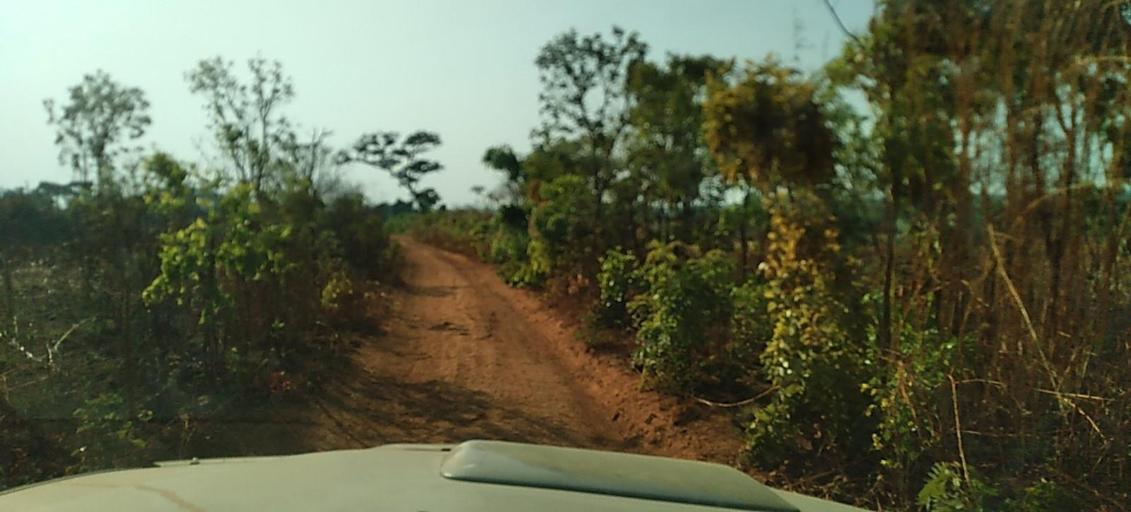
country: ZM
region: North-Western
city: Kasempa
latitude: -13.1835
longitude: 25.9504
